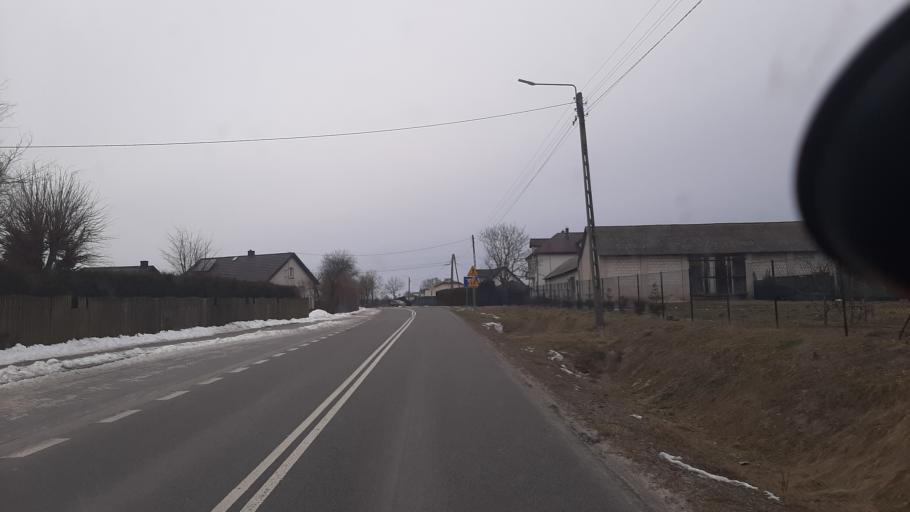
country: PL
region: Lublin Voivodeship
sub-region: Powiat lubartowski
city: Kamionka
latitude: 51.4911
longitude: 22.4344
